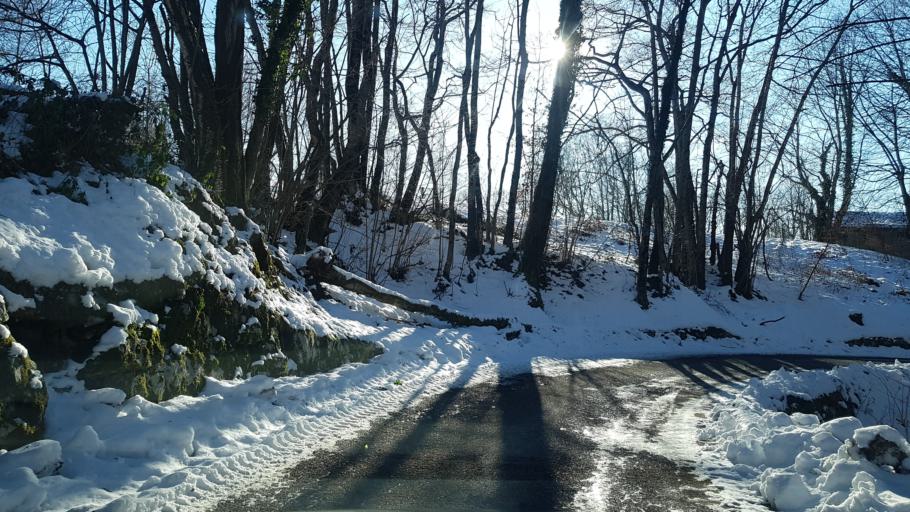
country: IT
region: Friuli Venezia Giulia
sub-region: Provincia di Udine
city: Forgaria nel Friuli
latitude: 46.2488
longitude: 12.9926
